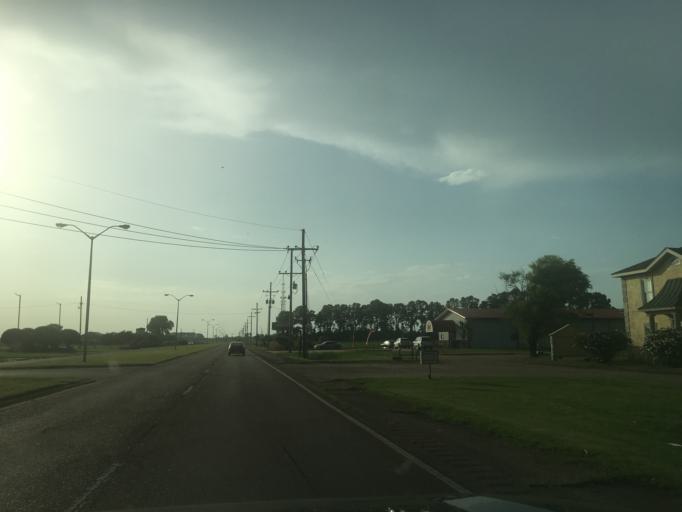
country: US
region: Mississippi
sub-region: Tunica County
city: North Tunica
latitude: 34.8325
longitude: -90.2846
